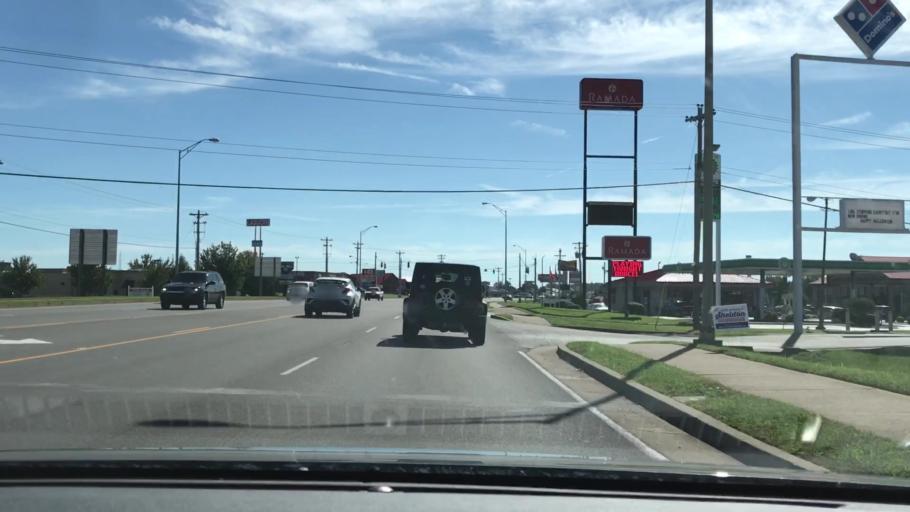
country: US
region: Kentucky
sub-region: Warren County
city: Plano
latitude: 36.9311
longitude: -86.4146
